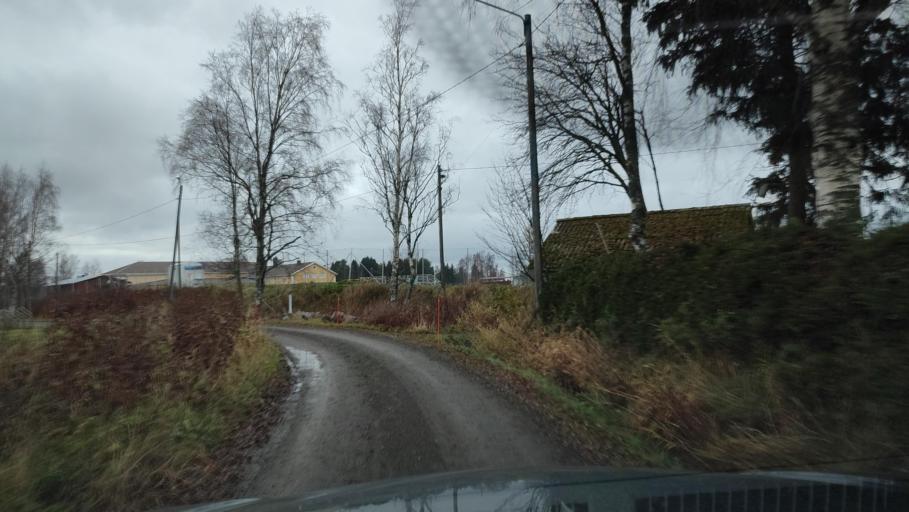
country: FI
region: Ostrobothnia
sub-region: Sydosterbotten
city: Kristinestad
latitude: 62.2536
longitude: 21.5312
